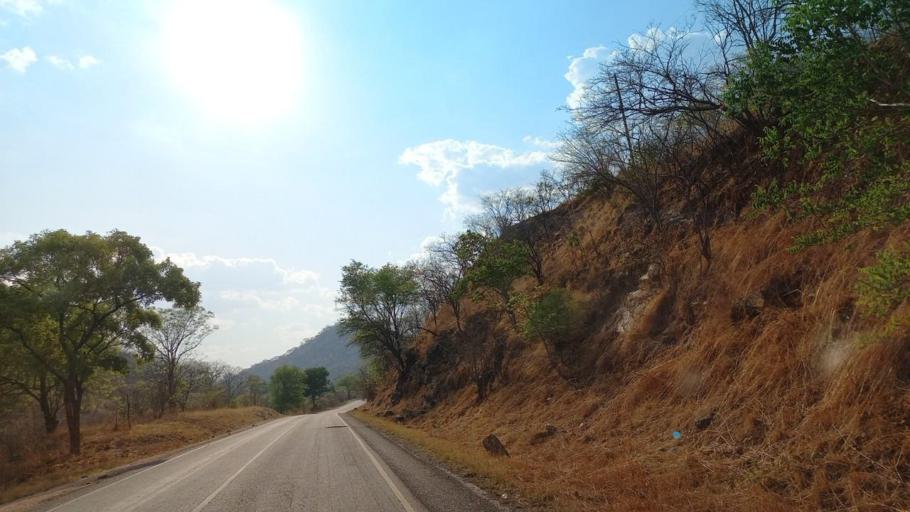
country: ZM
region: Lusaka
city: Luangwa
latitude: -14.9855
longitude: 30.1949
